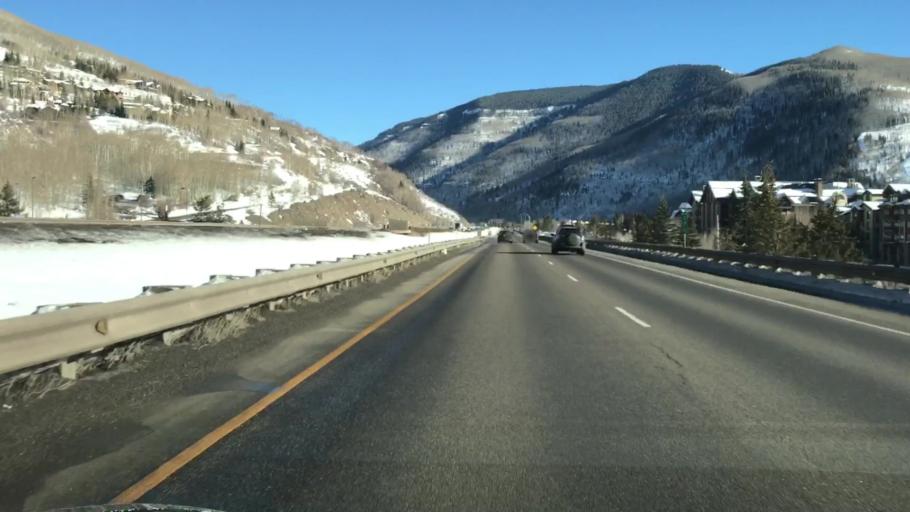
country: US
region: Colorado
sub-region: Eagle County
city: Vail
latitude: 39.6445
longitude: -106.3792
